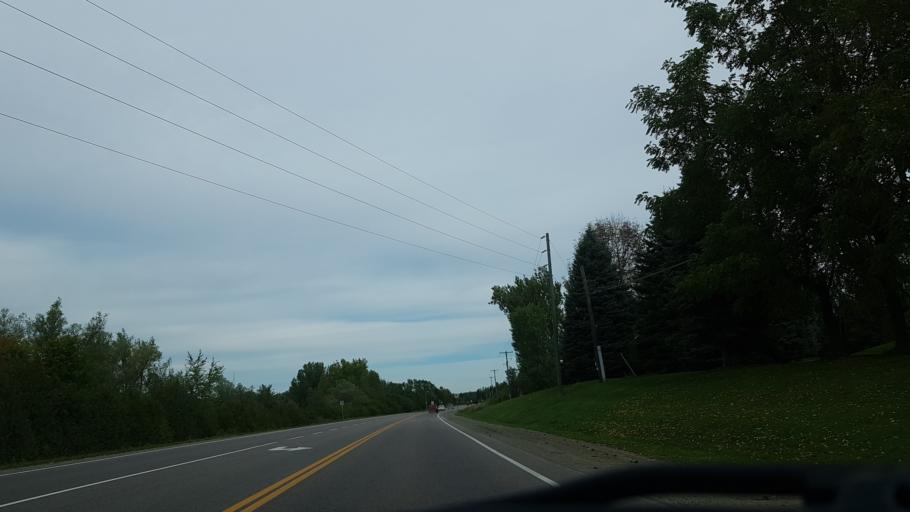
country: CA
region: Ontario
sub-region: Wellington County
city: Guelph
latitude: 43.6022
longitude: -80.2310
